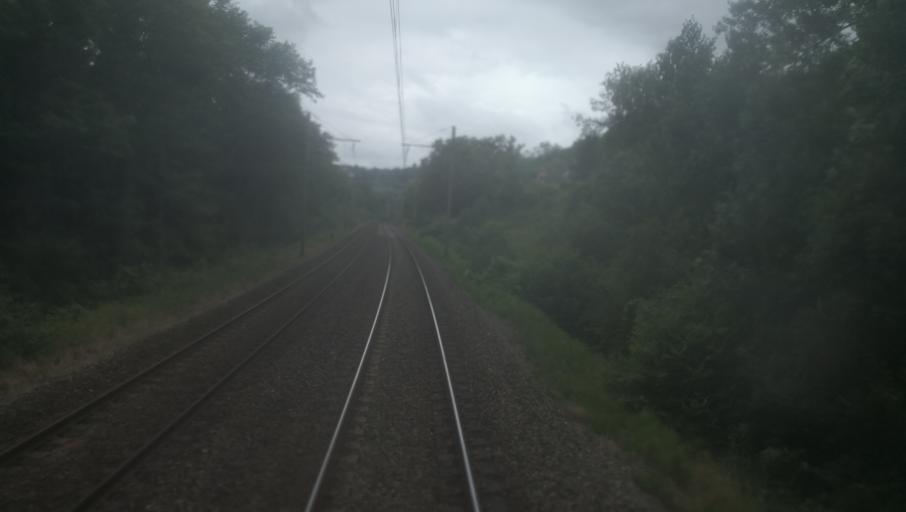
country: FR
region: Midi-Pyrenees
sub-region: Departement du Tarn-et-Garonne
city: Saint-Nicolas-de-la-Grave
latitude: 44.0924
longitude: 1.0348
